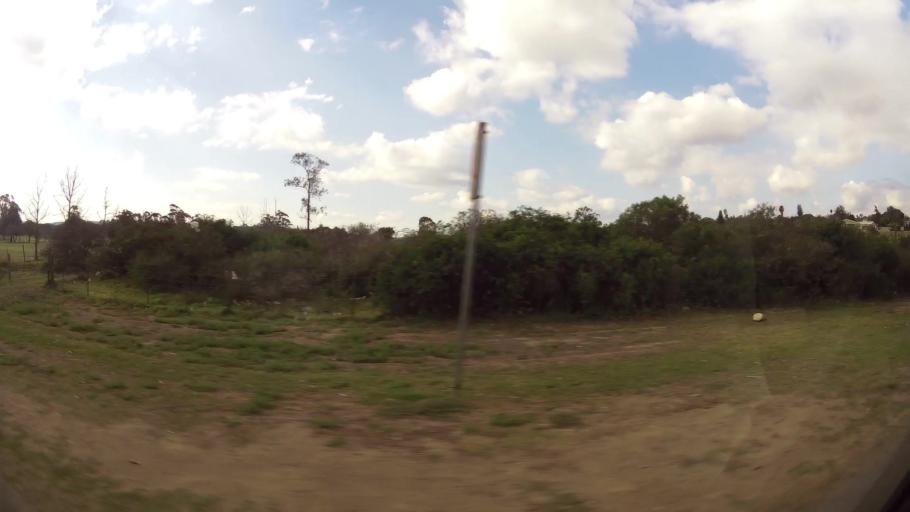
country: ZA
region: Eastern Cape
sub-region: Nelson Mandela Bay Metropolitan Municipality
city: Uitenhage
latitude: -33.7489
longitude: 25.4137
